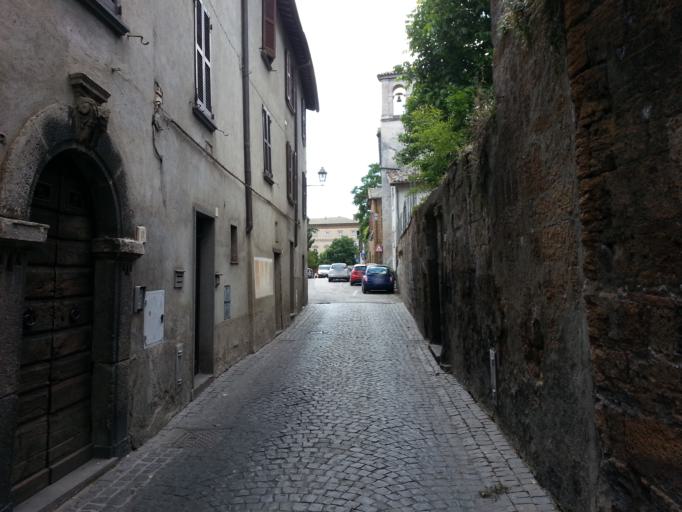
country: IT
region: Umbria
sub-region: Provincia di Terni
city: Orvieto
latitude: 42.7180
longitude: 12.1135
